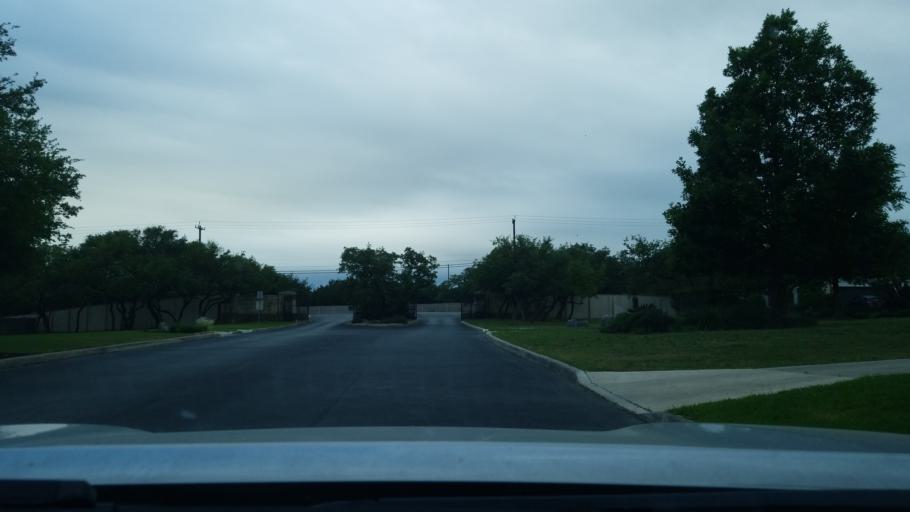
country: US
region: Texas
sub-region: Bexar County
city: Timberwood Park
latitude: 29.7093
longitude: -98.4948
